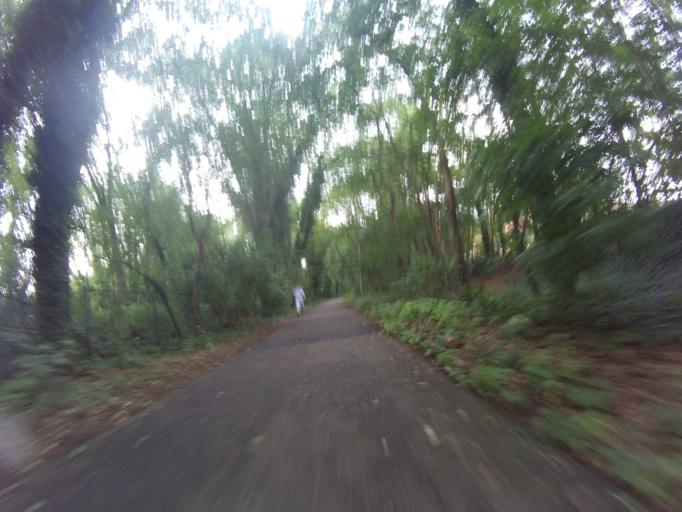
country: NL
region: Drenthe
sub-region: Gemeente Emmen
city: Emmen
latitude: 52.7839
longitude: 6.9151
